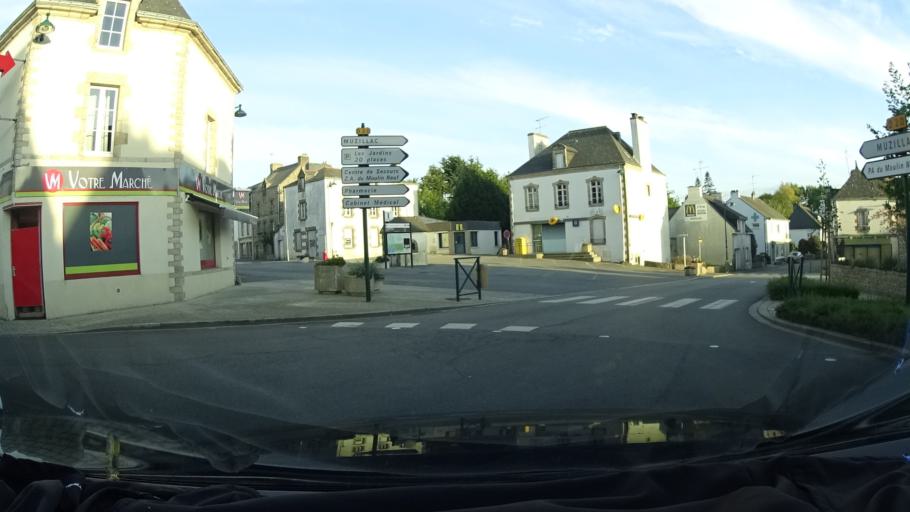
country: FR
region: Brittany
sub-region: Departement du Morbihan
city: Peaule
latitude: 47.5812
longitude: -2.3574
